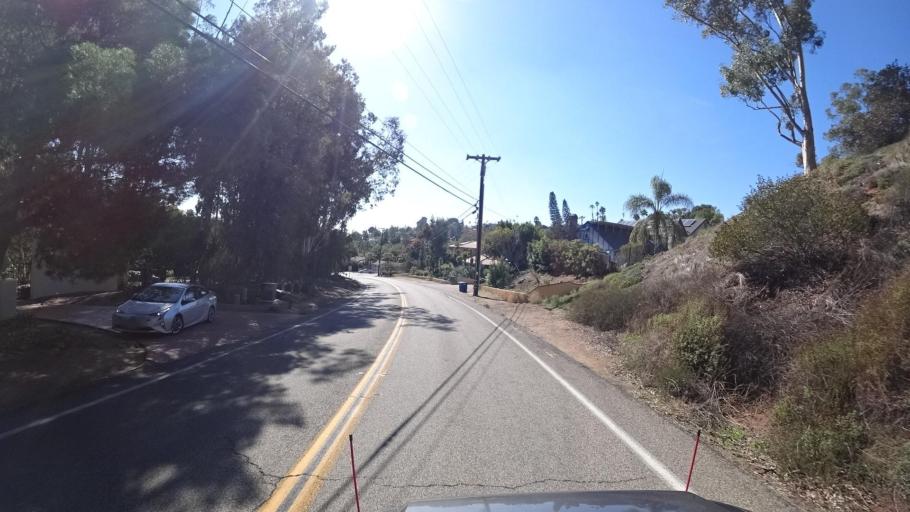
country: US
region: California
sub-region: San Diego County
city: Spring Valley
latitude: 32.7579
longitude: -116.9865
